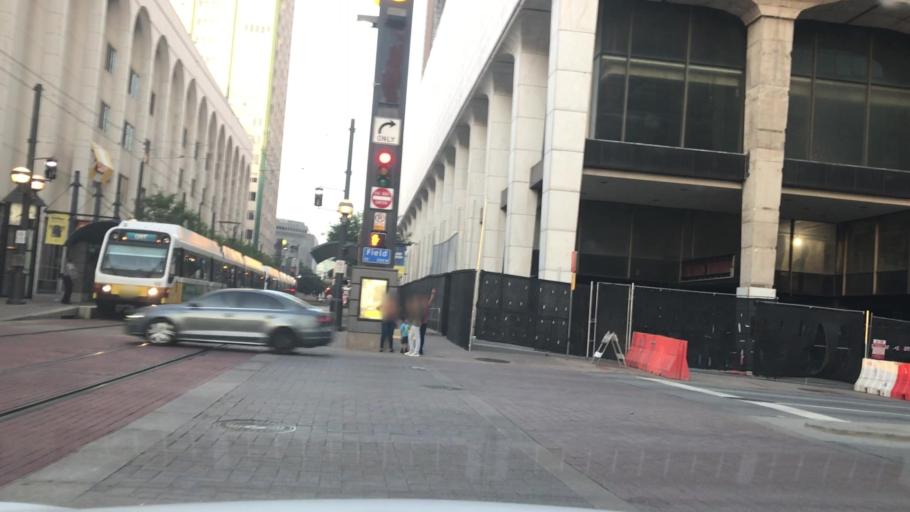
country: US
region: Texas
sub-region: Dallas County
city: Dallas
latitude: 32.7818
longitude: -96.8017
